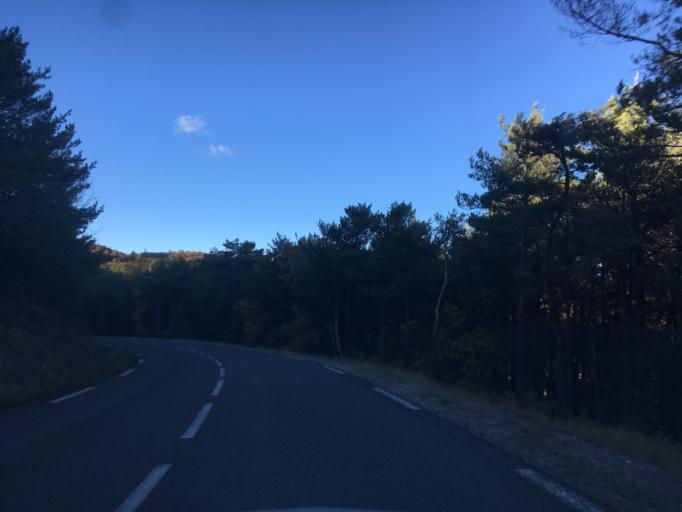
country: FR
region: Provence-Alpes-Cote d'Azur
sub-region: Departement du Var
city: Montferrat
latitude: 43.7192
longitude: 6.5030
